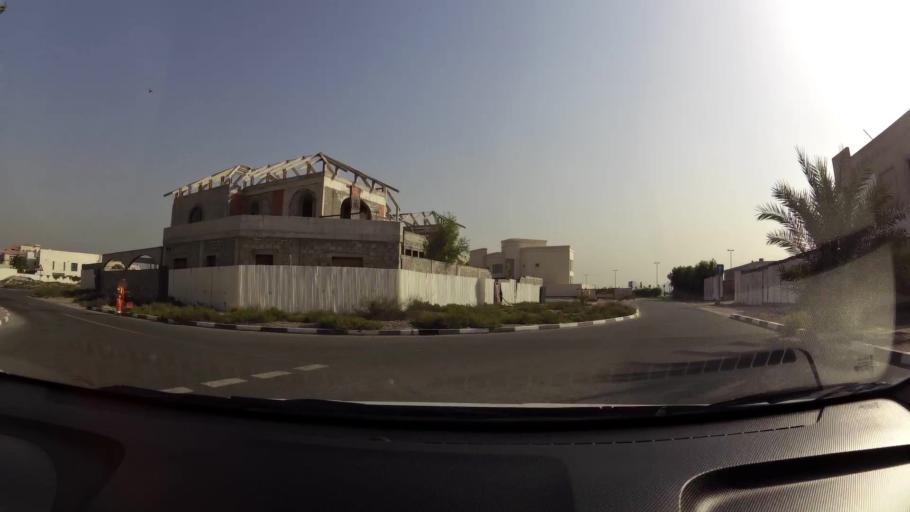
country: AE
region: Ash Shariqah
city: Sharjah
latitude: 25.3086
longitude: 55.3462
